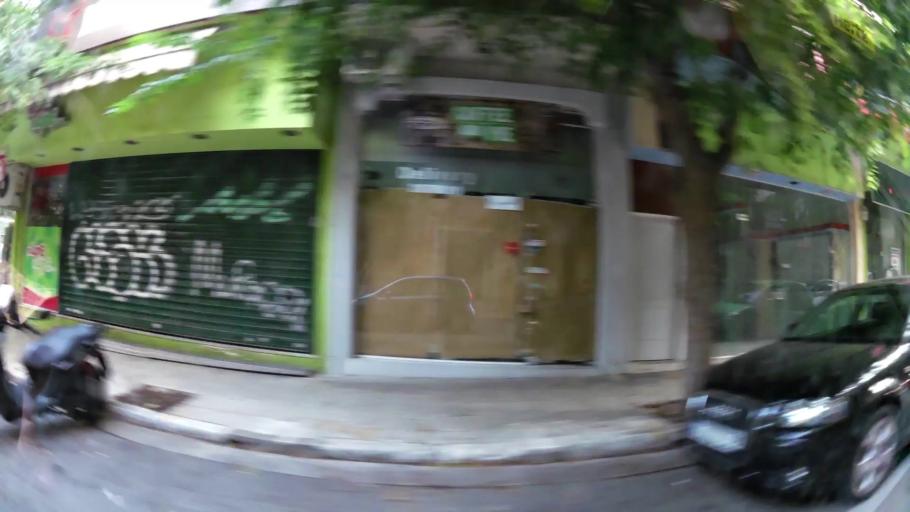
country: GR
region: Attica
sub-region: Nomarchia Athinas
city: Kaisariani
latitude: 37.9811
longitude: 23.7606
